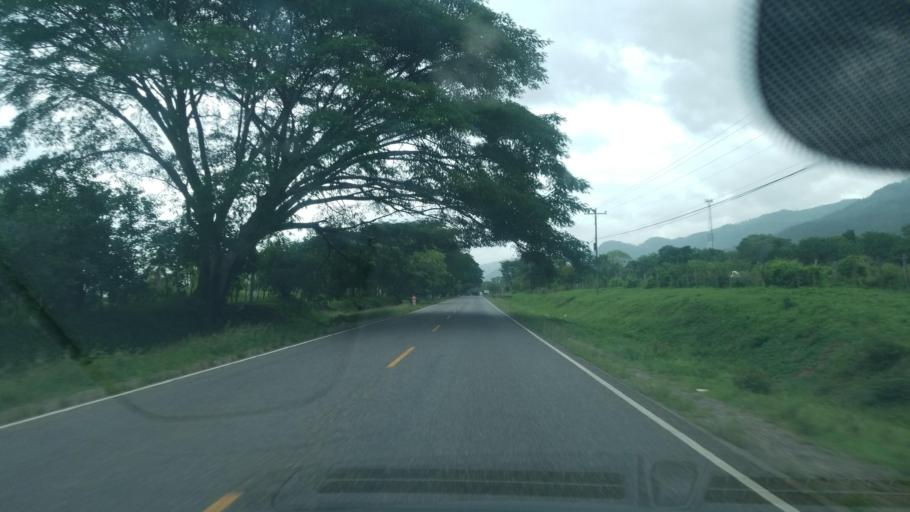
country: HN
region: Ocotepeque
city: Antigua Ocotepeque
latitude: 14.3975
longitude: -89.1991
